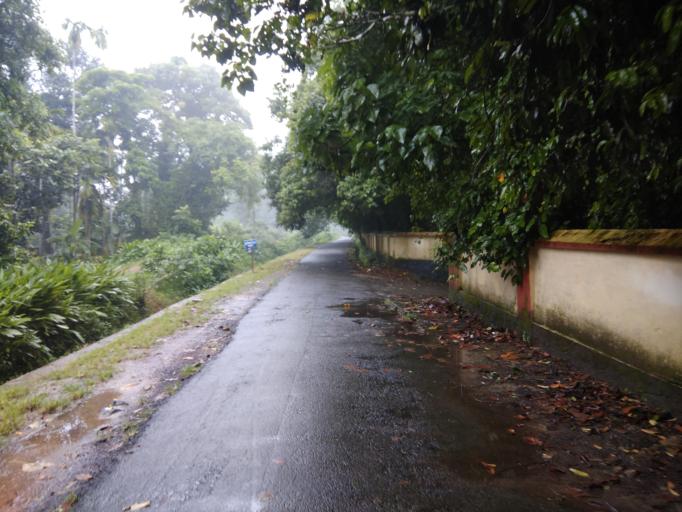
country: IN
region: Kerala
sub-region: Ernakulam
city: Perumpavur
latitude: 10.1103
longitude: 76.5000
